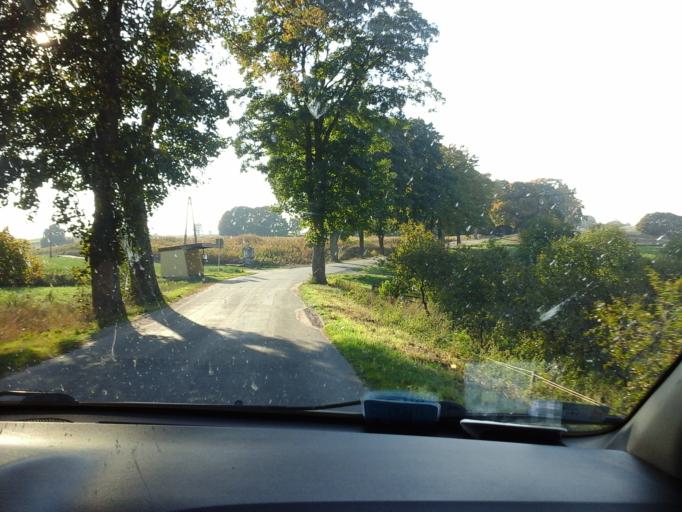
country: PL
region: Kujawsko-Pomorskie
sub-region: Powiat brodnicki
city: Brzozie
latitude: 53.2950
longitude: 19.6461
